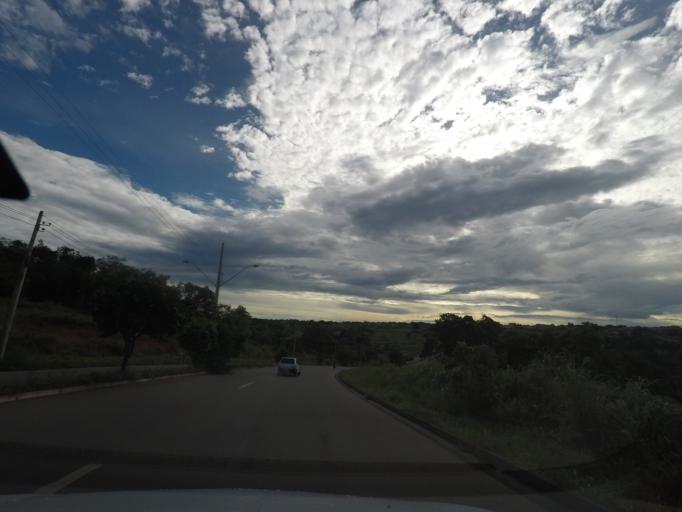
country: BR
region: Goias
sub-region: Aparecida De Goiania
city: Aparecida de Goiania
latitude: -16.7849
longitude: -49.3789
